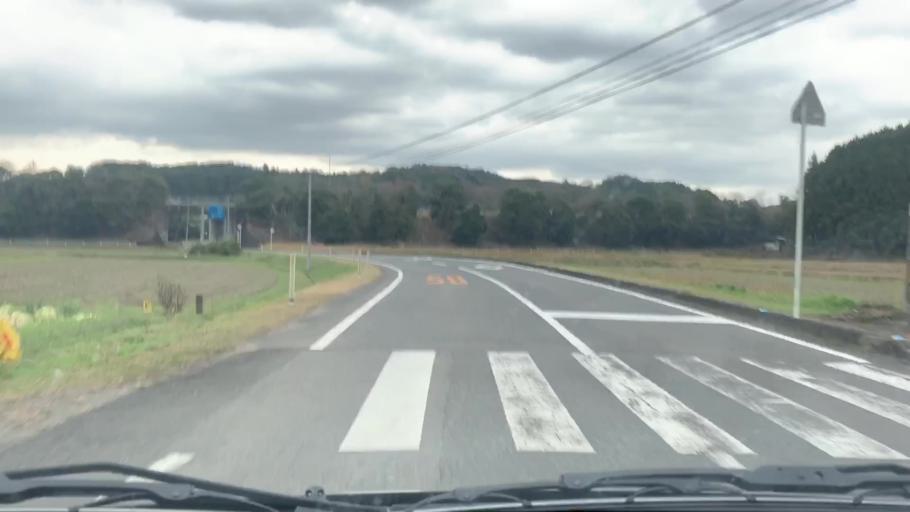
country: JP
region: Saga Prefecture
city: Ureshinomachi-shimojuku
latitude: 33.1273
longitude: 129.9803
